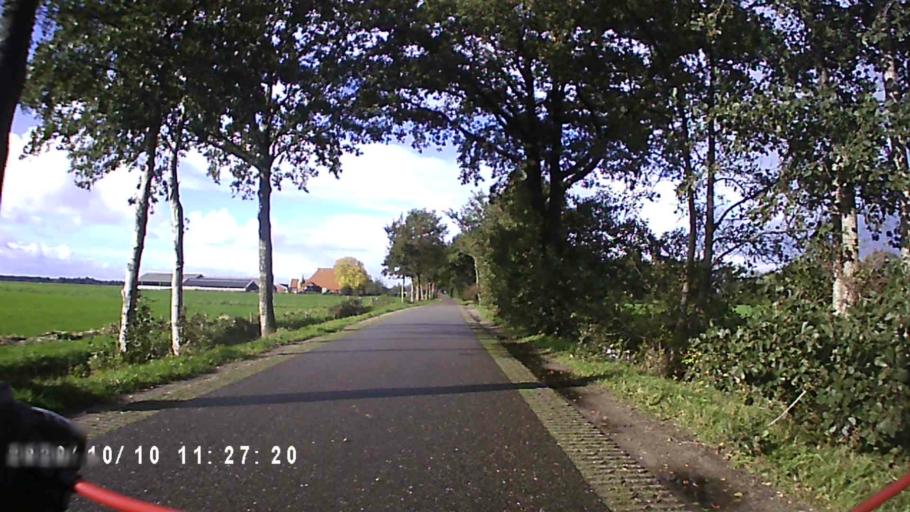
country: NL
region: Friesland
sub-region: Gemeente Smallingerland
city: Drachtstercompagnie
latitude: 53.0877
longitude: 6.1593
